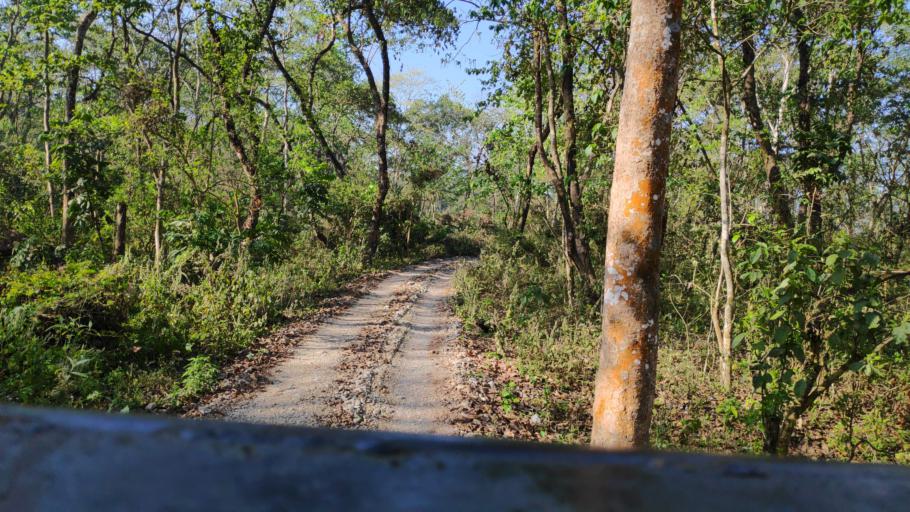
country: NP
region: Central Region
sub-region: Narayani Zone
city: Bharatpur
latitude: 27.5611
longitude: 84.5318
